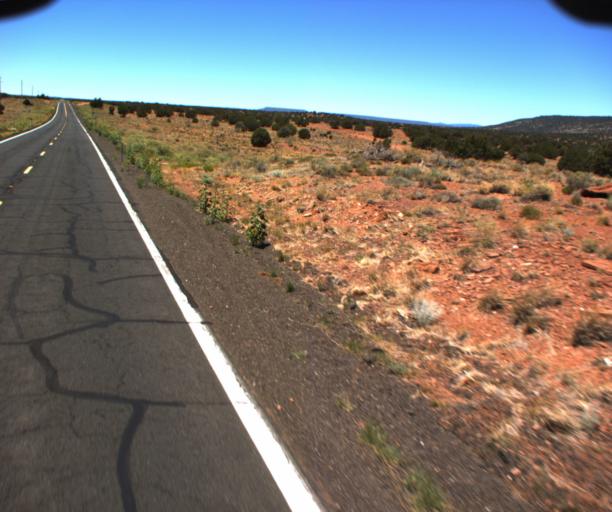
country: US
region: Arizona
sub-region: Coconino County
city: LeChee
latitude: 34.8616
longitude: -110.9142
